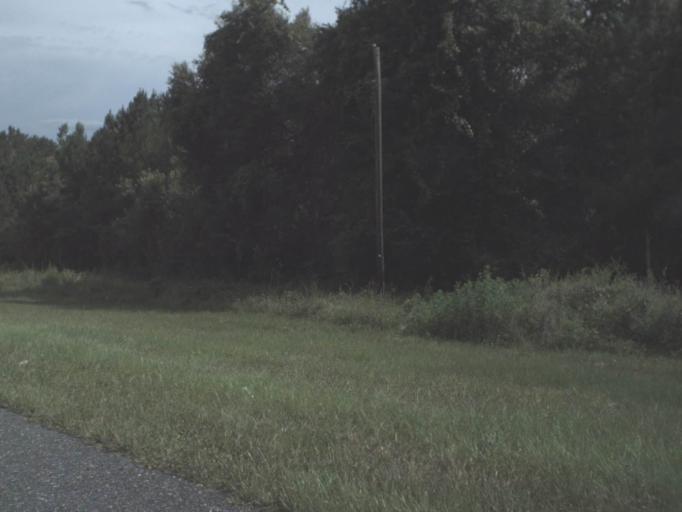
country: US
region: Florida
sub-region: Levy County
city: Inglis
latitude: 29.2076
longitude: -82.6955
